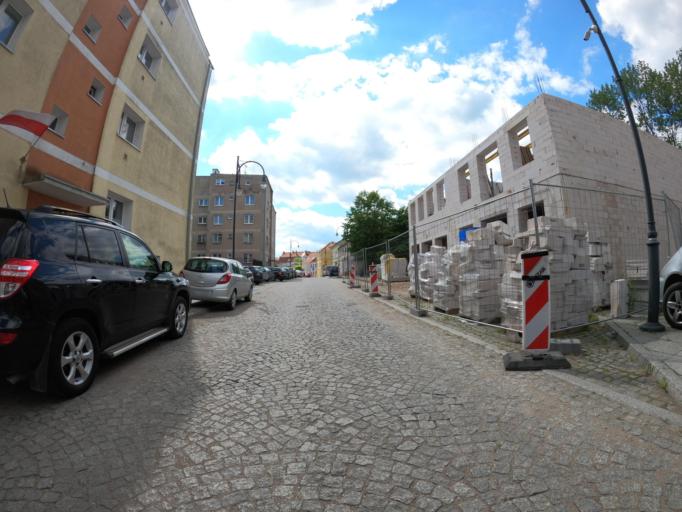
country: PL
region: Warmian-Masurian Voivodeship
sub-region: Powiat lidzbarski
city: Lidzbark Warminski
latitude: 54.1268
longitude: 20.5804
